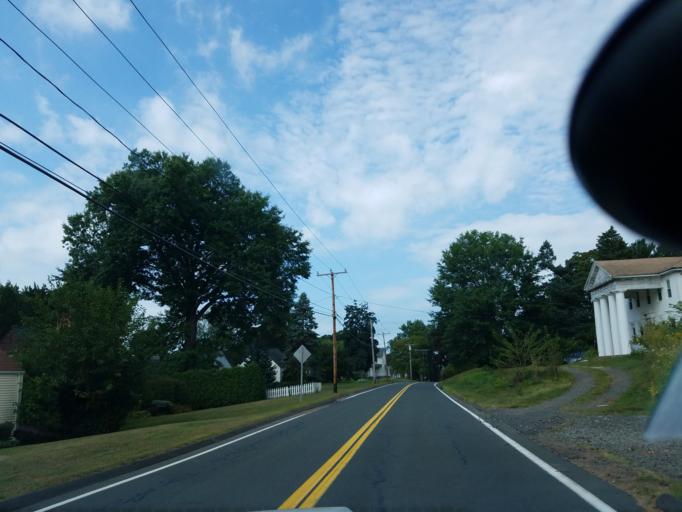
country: US
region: Connecticut
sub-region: Hartford County
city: Wethersfield
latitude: 41.6783
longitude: -72.6457
